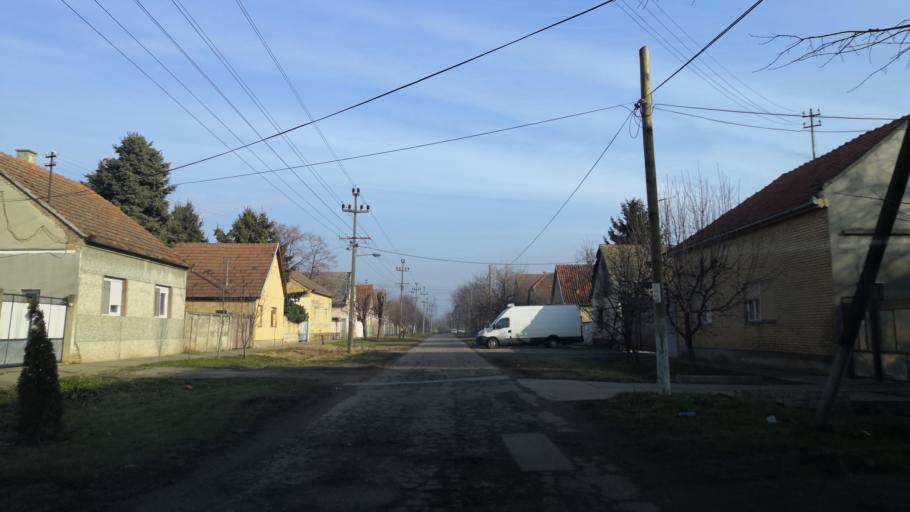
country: RS
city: Rumenka
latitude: 45.2959
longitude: 19.7470
